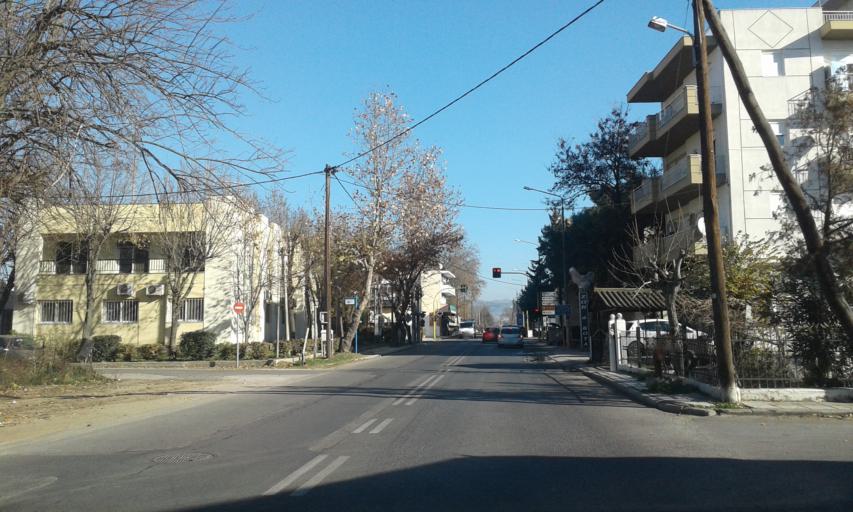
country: GR
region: Central Macedonia
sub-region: Nomos Thessalonikis
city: Lagkadas
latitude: 40.7465
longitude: 23.0707
